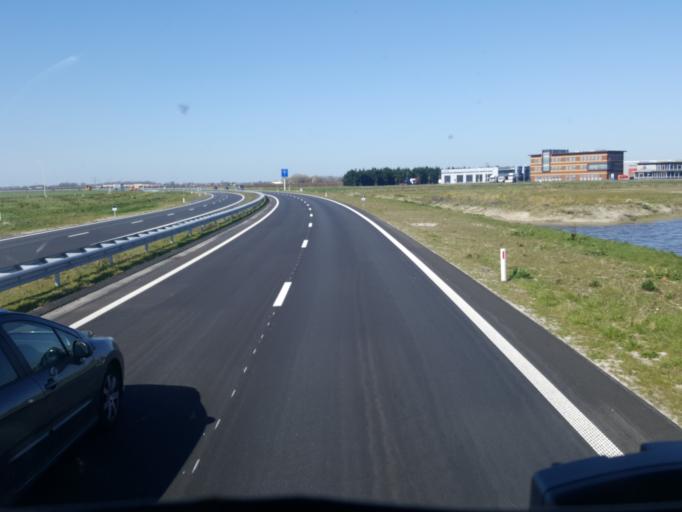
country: NL
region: North Holland
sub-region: Gemeente Medemblik
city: Medemblik
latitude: 52.6968
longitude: 5.1506
